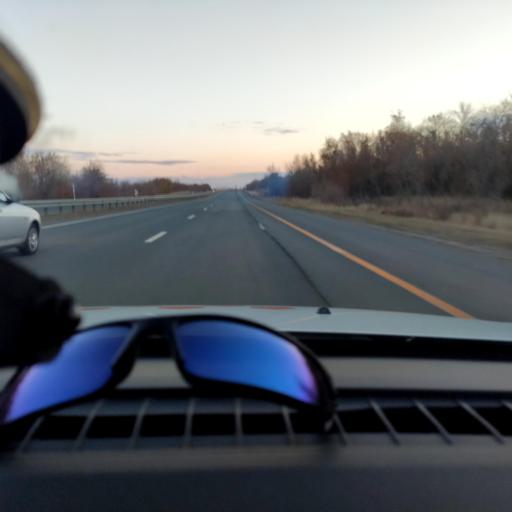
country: RU
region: Samara
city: Novokuybyshevsk
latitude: 53.0416
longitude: 50.0030
